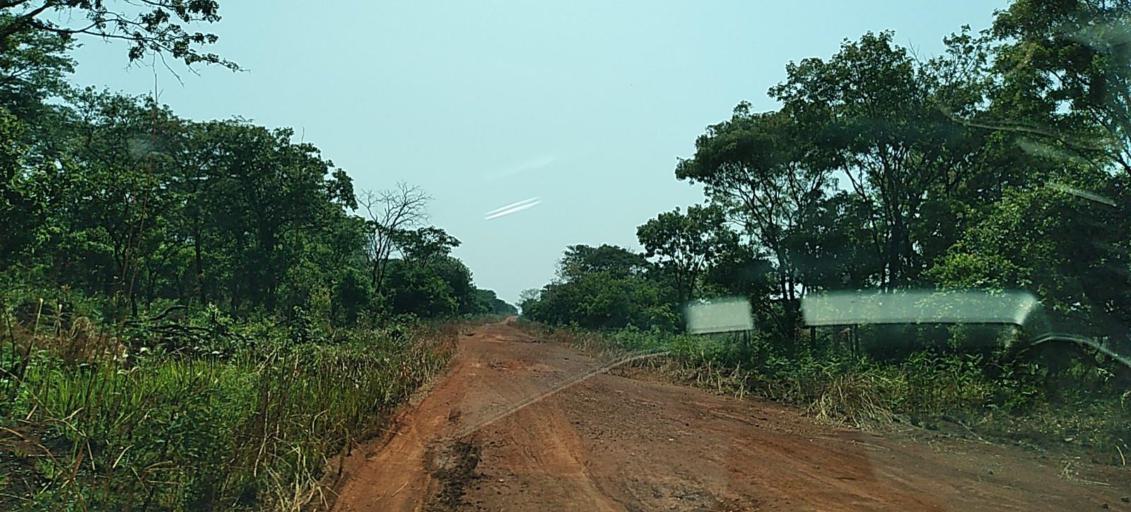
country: ZM
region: North-Western
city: Kansanshi
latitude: -12.0077
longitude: 26.5192
